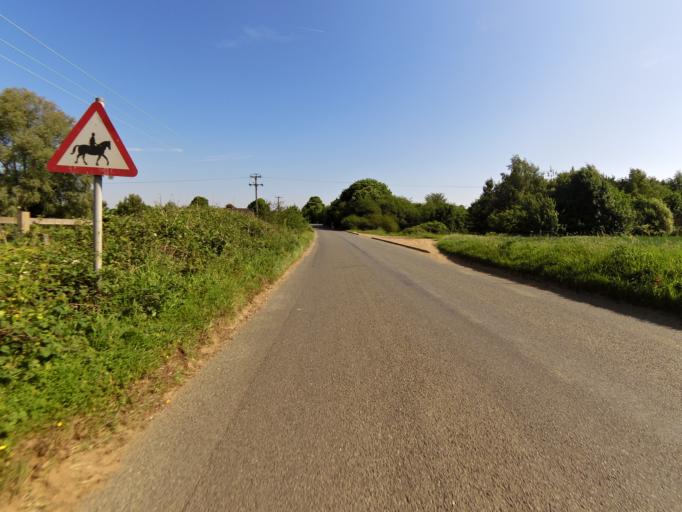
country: GB
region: England
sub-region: Suffolk
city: Bramford
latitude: 52.0988
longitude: 1.1060
